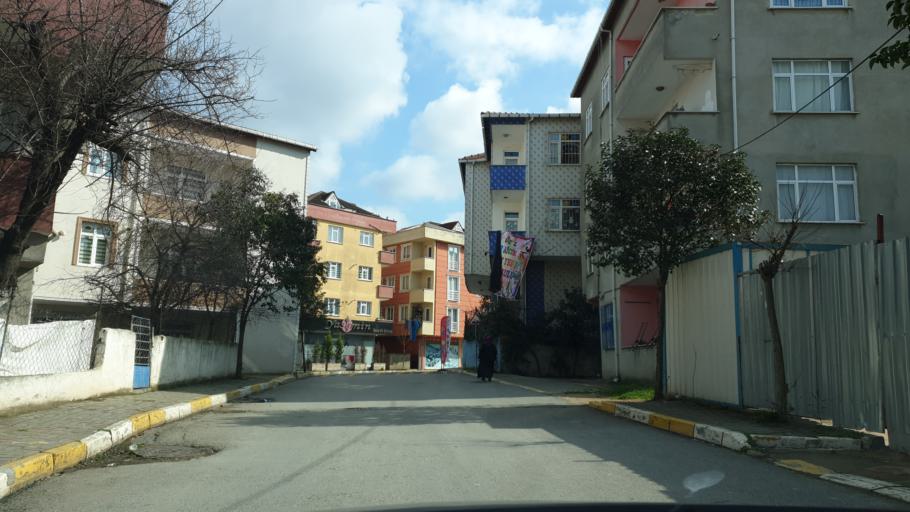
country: TR
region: Istanbul
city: Icmeler
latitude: 40.8671
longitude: 29.3053
